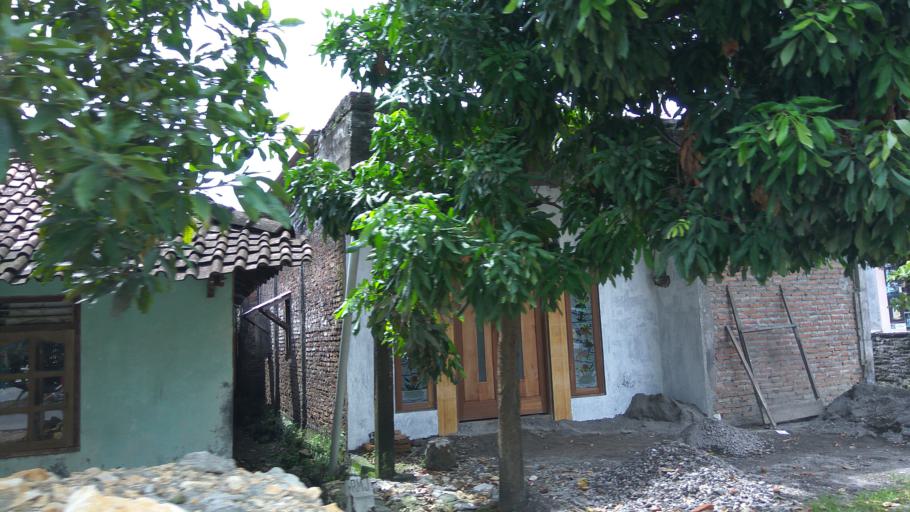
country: ID
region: Central Java
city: Mranggen
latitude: -7.0659
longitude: 110.6655
